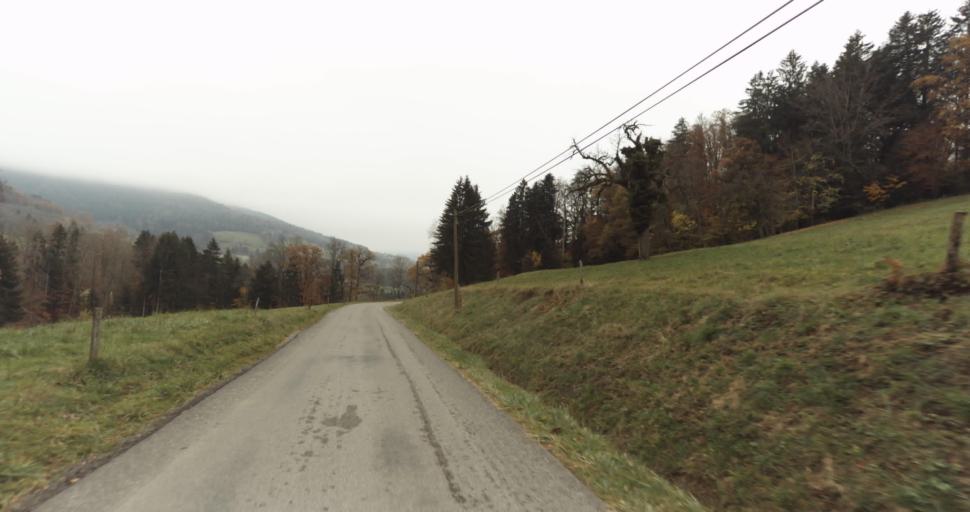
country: FR
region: Rhone-Alpes
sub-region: Departement de la Haute-Savoie
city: Villaz
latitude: 45.9738
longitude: 6.2132
